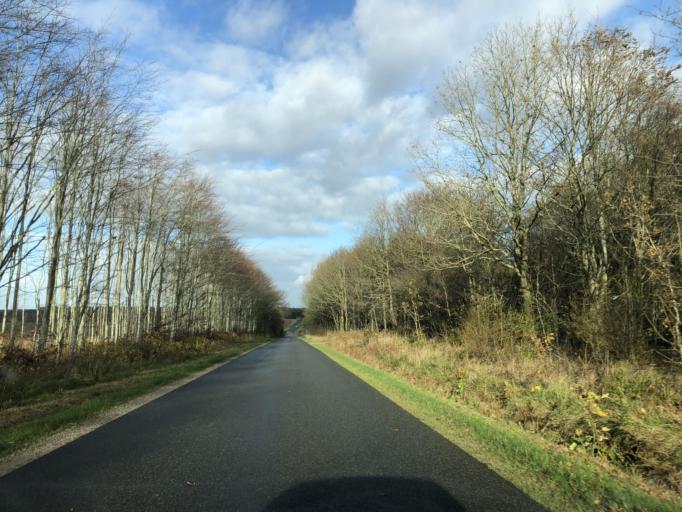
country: DK
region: Central Jutland
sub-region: Holstebro Kommune
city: Ulfborg
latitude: 56.1874
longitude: 8.4206
